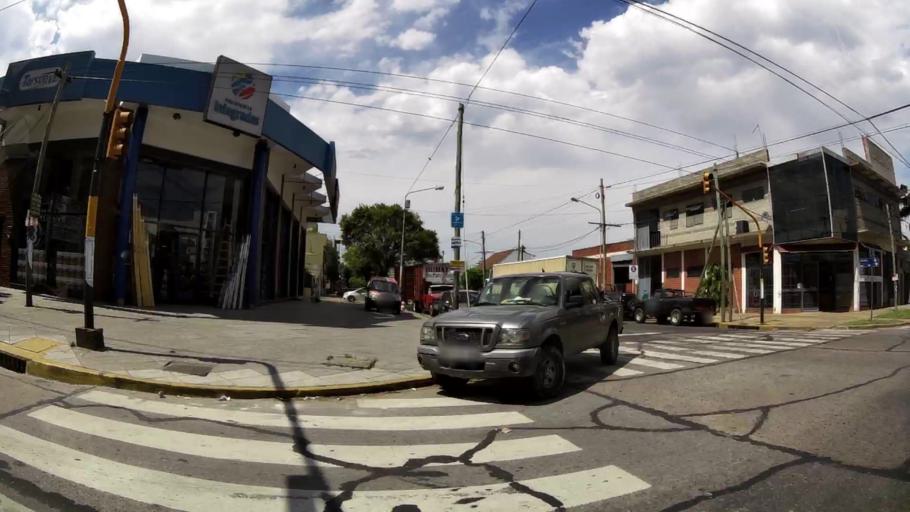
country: AR
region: Buenos Aires
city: San Justo
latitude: -34.6781
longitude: -58.5545
